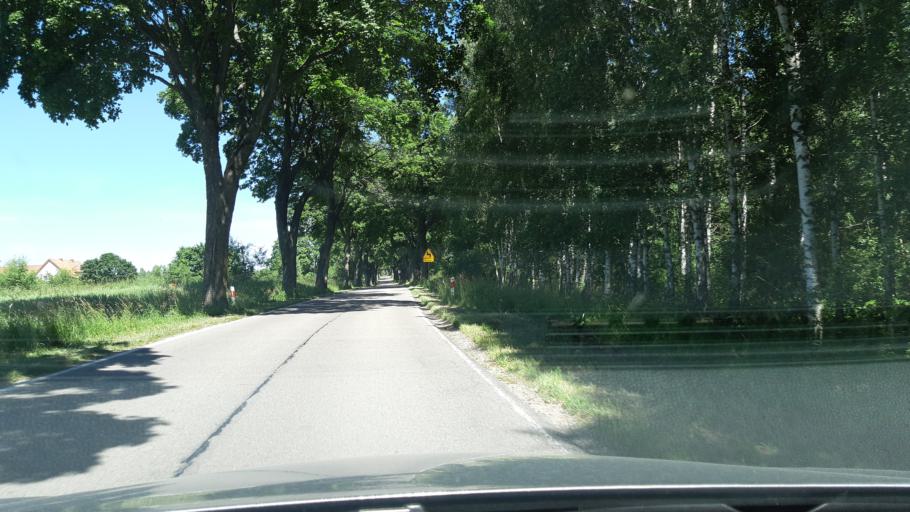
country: PL
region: Warmian-Masurian Voivodeship
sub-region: Powiat mragowski
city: Mikolajki
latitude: 53.8861
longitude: 21.6553
